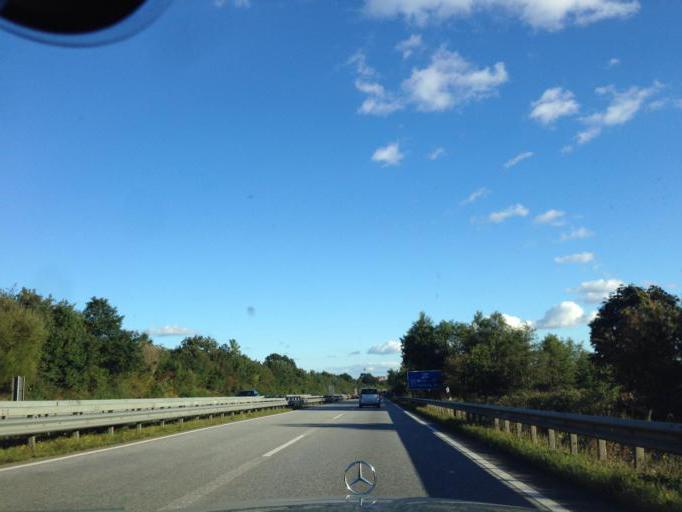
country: DE
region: Schleswig-Holstein
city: Schackendorf
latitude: 53.9559
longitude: 10.2668
